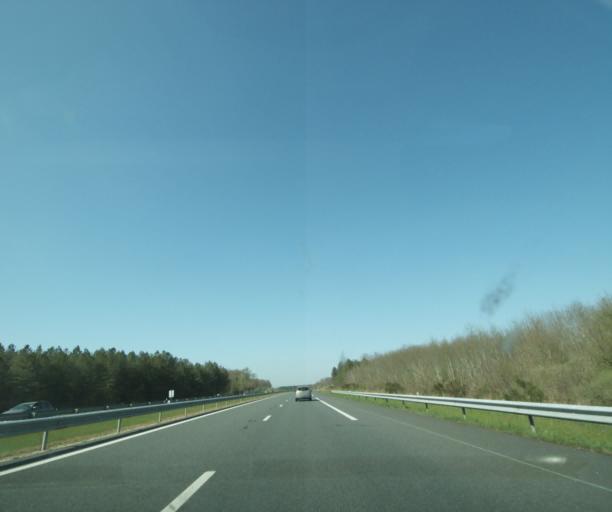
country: FR
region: Centre
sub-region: Departement du Loiret
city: Nogent-sur-Vernisson
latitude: 47.7814
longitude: 2.7085
